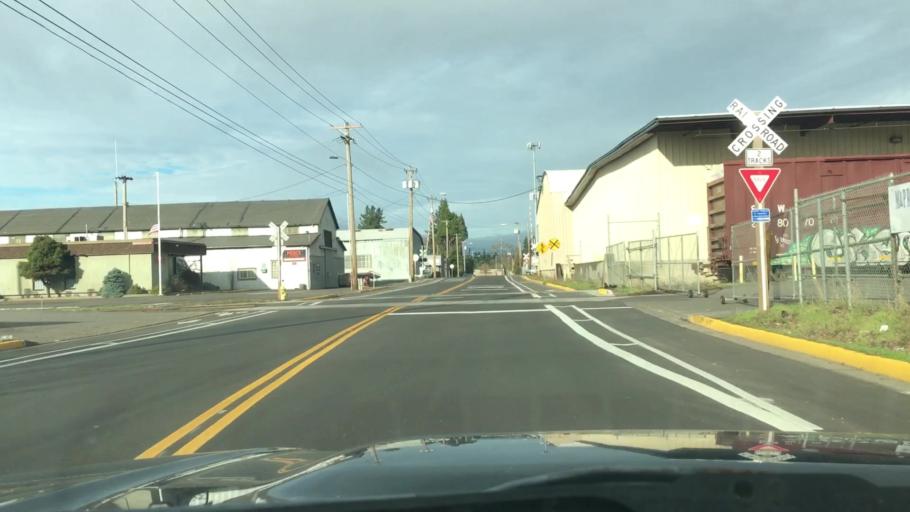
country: US
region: Oregon
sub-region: Lane County
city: Eugene
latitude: 44.0592
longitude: -123.1227
